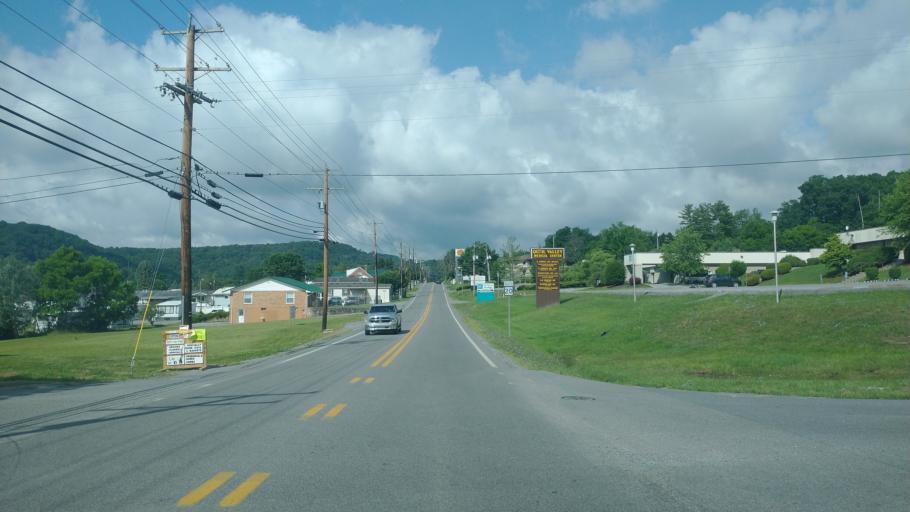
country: US
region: West Virginia
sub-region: Mercer County
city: Princeton
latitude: 37.3653
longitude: -81.1169
